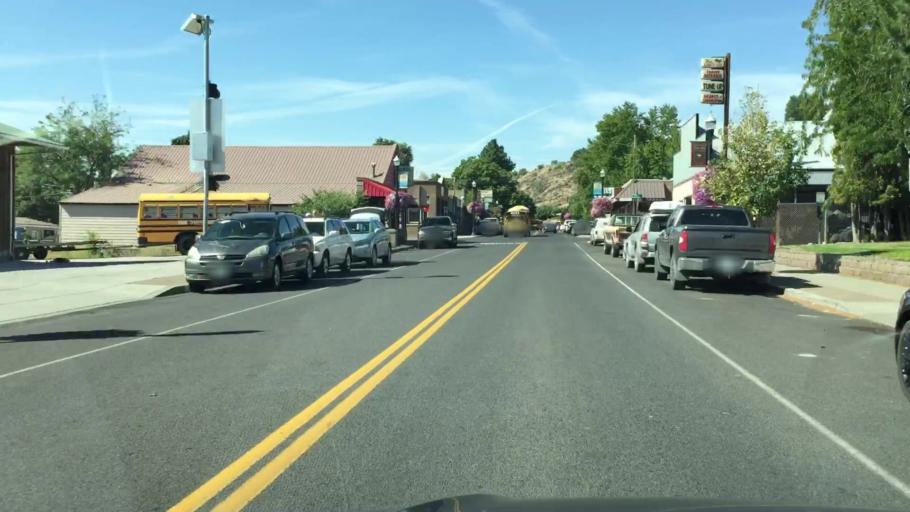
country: US
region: Oregon
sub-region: Wasco County
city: The Dalles
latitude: 45.1756
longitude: -121.0800
